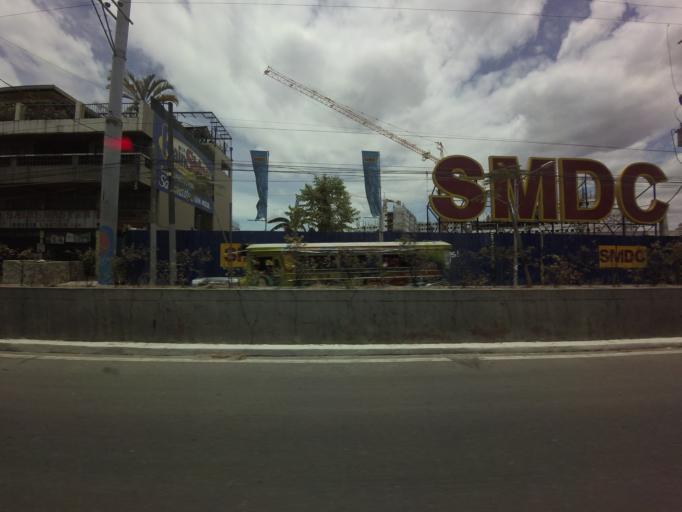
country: PH
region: Metro Manila
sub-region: Marikina
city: Calumpang
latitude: 14.6139
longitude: 121.1025
